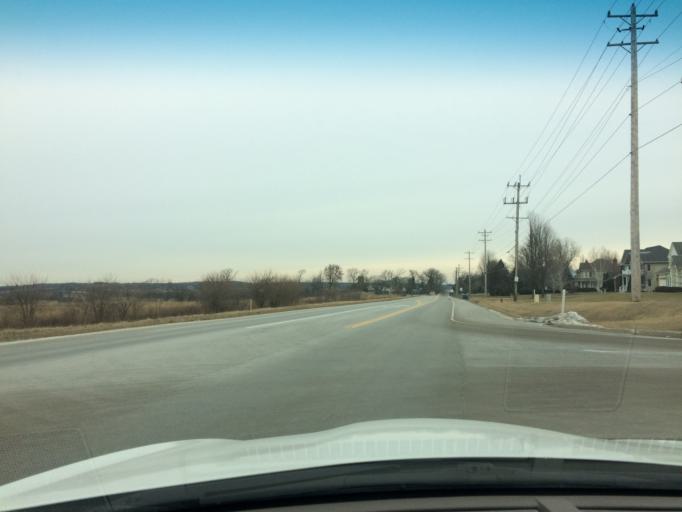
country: US
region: Illinois
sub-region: Kane County
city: Geneva
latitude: 41.8849
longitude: -88.3597
